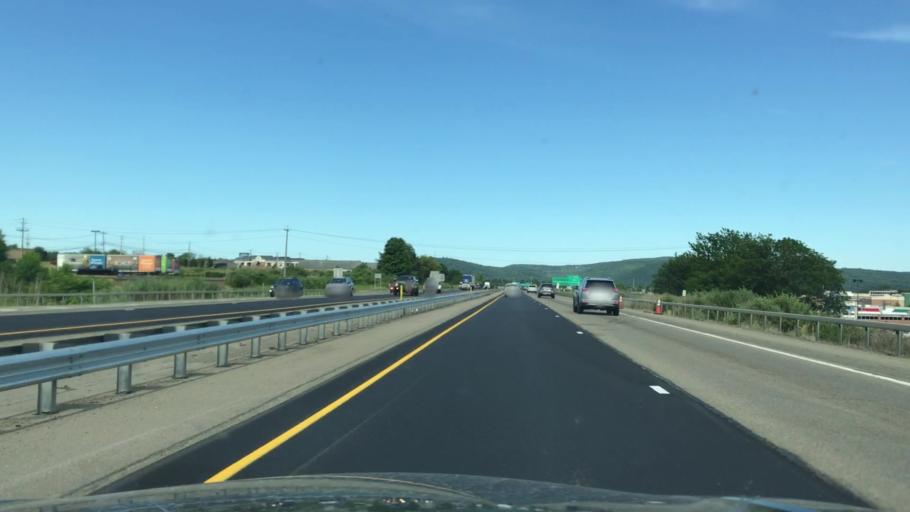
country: US
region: New York
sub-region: Chemung County
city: Horseheads
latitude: 42.1595
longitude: -76.8633
